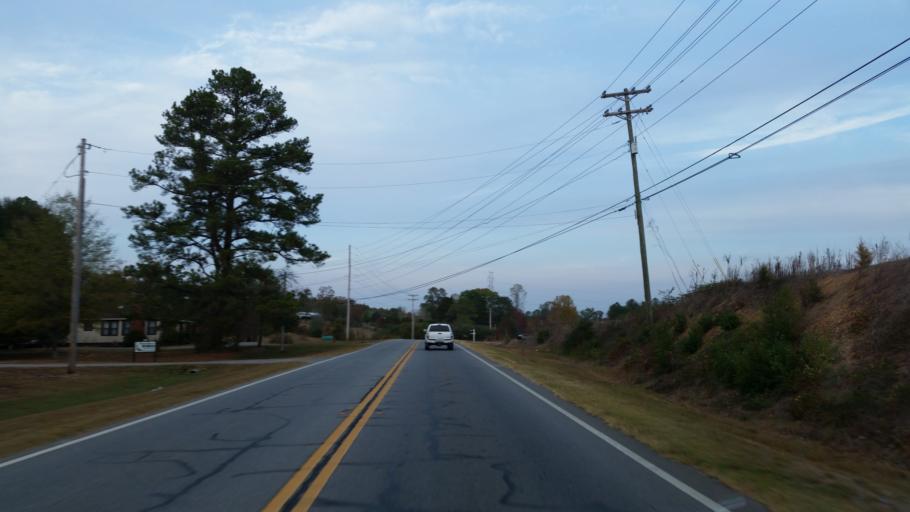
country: US
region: Georgia
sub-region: Gordon County
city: Calhoun
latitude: 34.5981
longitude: -84.9284
